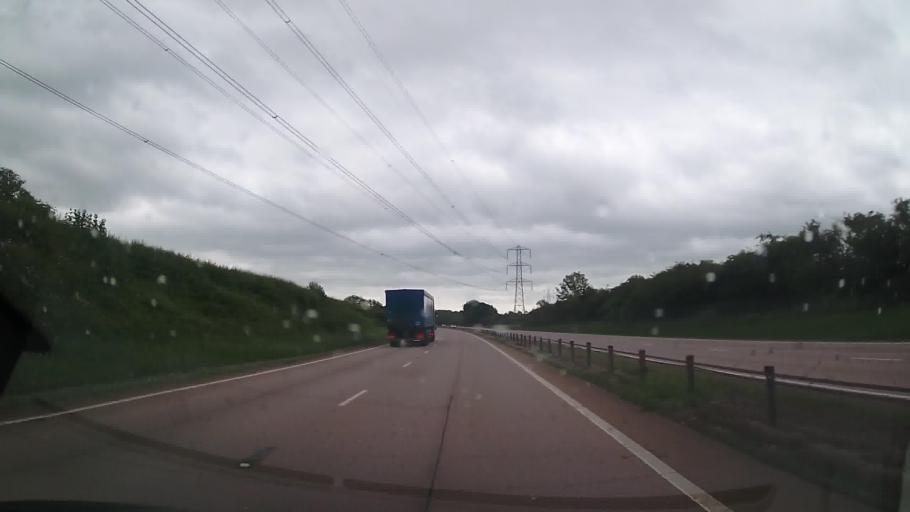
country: GB
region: England
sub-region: Staffordshire
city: Uttoxeter
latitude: 52.9236
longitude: -1.9348
